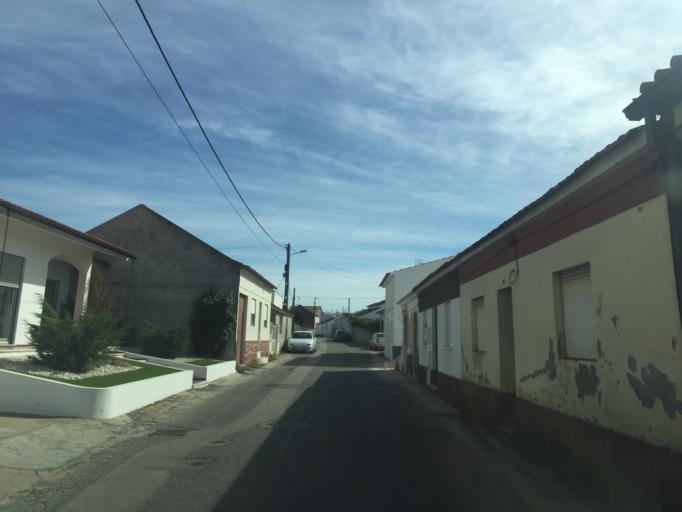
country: PT
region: Coimbra
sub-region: Figueira da Foz
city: Lavos
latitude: 40.0900
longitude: -8.8368
